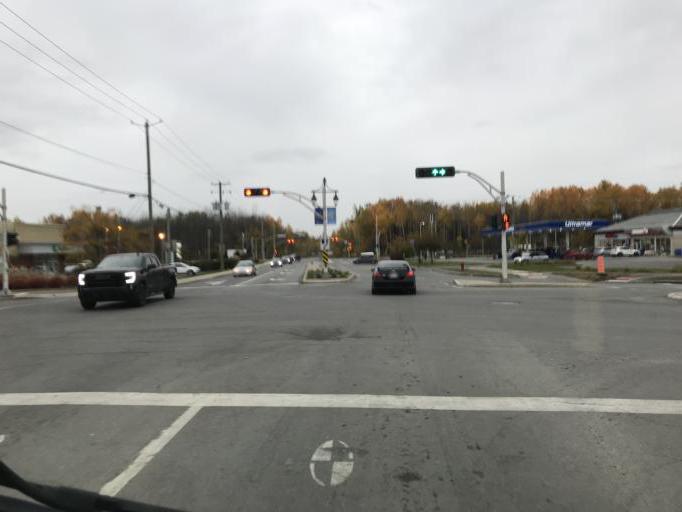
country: CA
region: Quebec
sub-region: Lanaudiere
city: Lorraine
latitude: 45.6890
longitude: -73.7826
